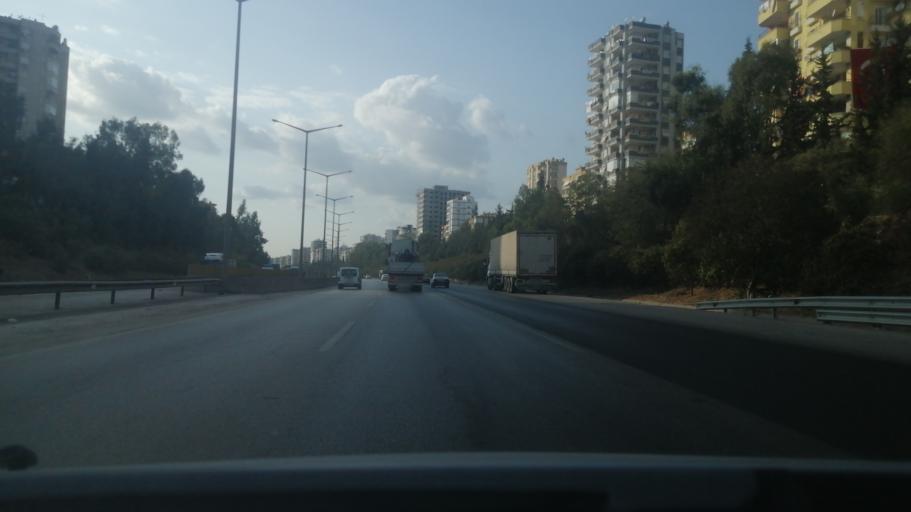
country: TR
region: Adana
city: Adana
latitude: 37.0314
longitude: 35.3090
